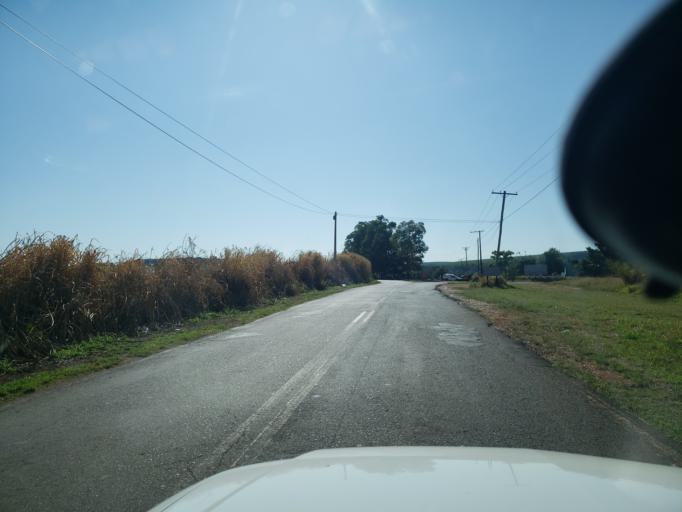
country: BR
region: Sao Paulo
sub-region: Moji-Guacu
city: Mogi-Gaucu
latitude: -22.3372
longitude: -46.8841
